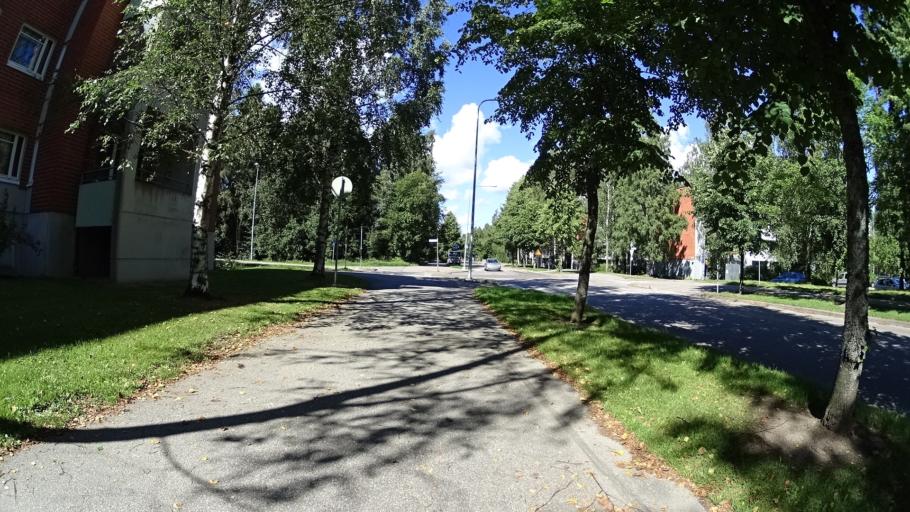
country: FI
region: Uusimaa
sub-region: Helsinki
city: Koukkuniemi
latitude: 60.1532
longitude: 24.7407
